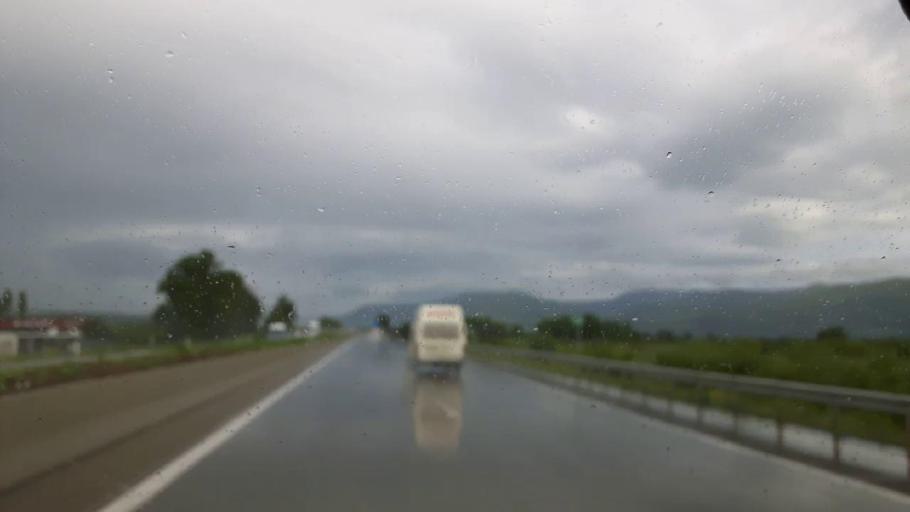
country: GE
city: Agara
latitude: 42.0358
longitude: 43.9399
